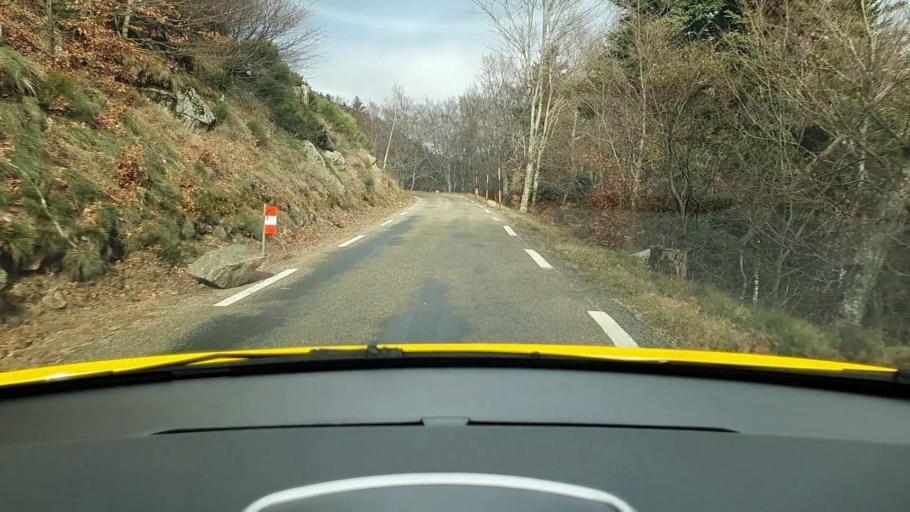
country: FR
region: Languedoc-Roussillon
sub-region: Departement du Gard
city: Branoux-les-Taillades
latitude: 44.3608
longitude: 3.9181
